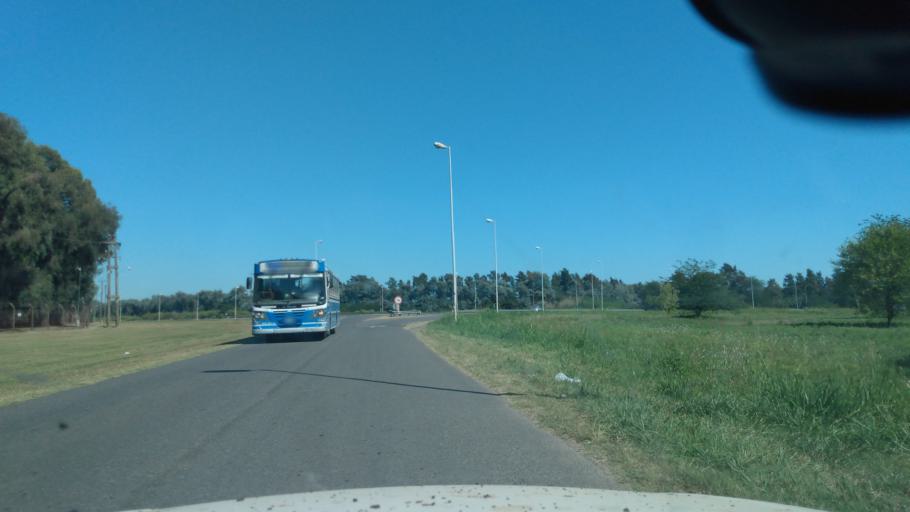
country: AR
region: Buenos Aires
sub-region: Partido de Lujan
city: Lujan
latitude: -34.5090
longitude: -59.0911
